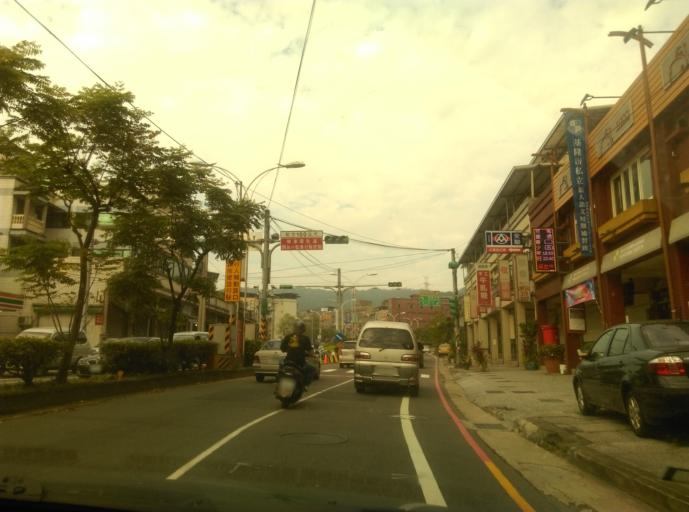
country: TW
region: Taiwan
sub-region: Keelung
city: Keelung
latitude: 25.1544
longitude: 121.6969
